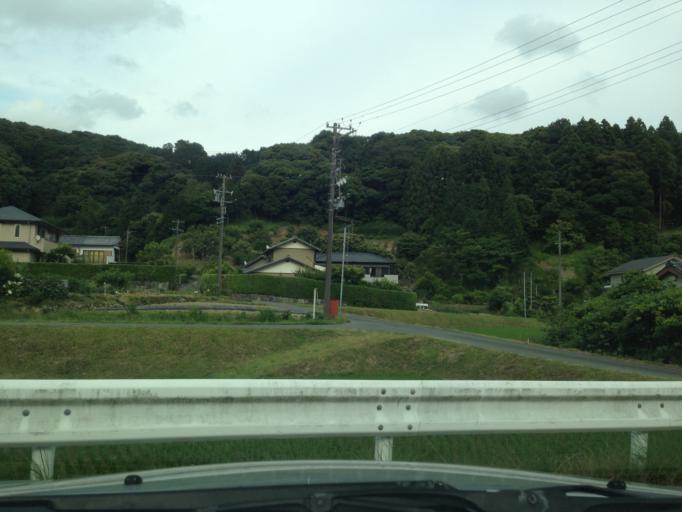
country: JP
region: Shizuoka
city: Kakegawa
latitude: 34.7277
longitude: 138.0235
